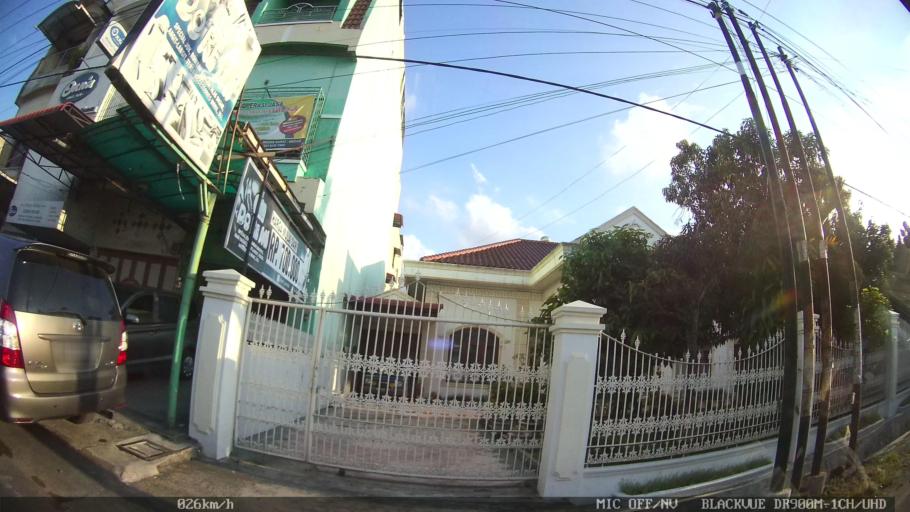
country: ID
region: North Sumatra
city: Medan
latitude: 3.6041
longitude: 98.6665
